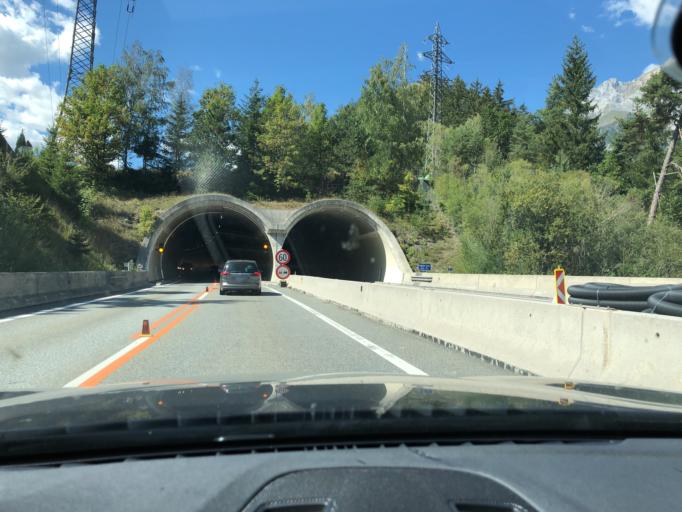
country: AT
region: Tyrol
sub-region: Politischer Bezirk Landeck
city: Grins
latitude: 47.1383
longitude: 10.5288
